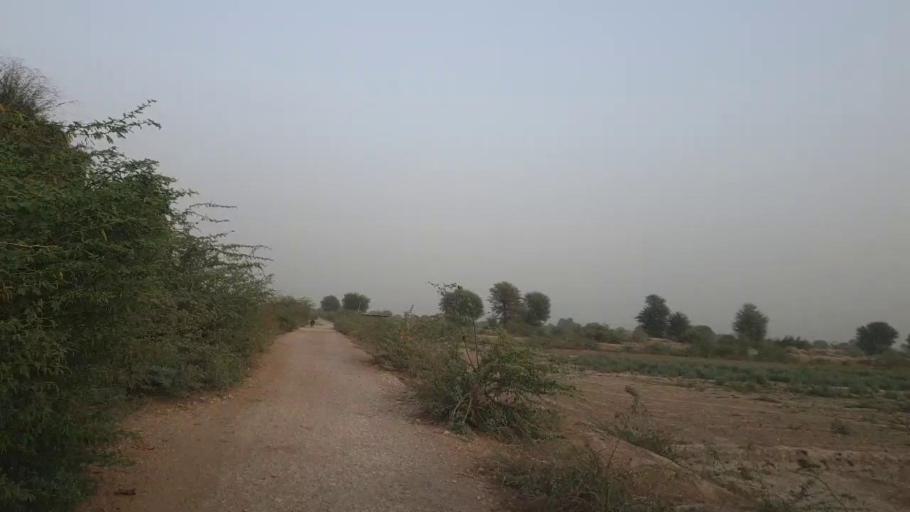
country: PK
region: Sindh
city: Kunri
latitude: 25.1194
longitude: 69.5504
